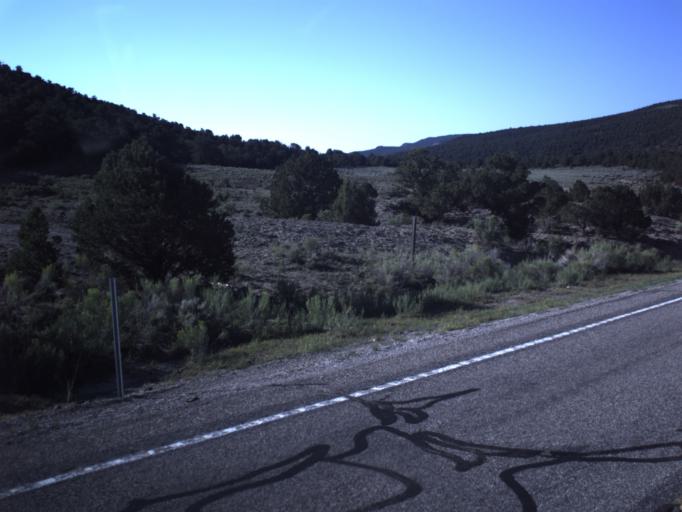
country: US
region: Utah
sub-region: Wayne County
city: Loa
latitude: 38.6771
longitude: -111.4012
